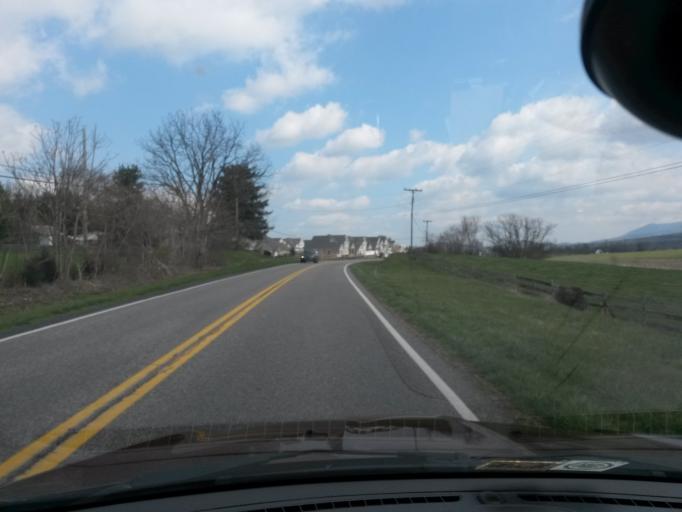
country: US
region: Virginia
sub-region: Rockingham County
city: Massanetta Springs
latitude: 38.3852
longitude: -78.8164
